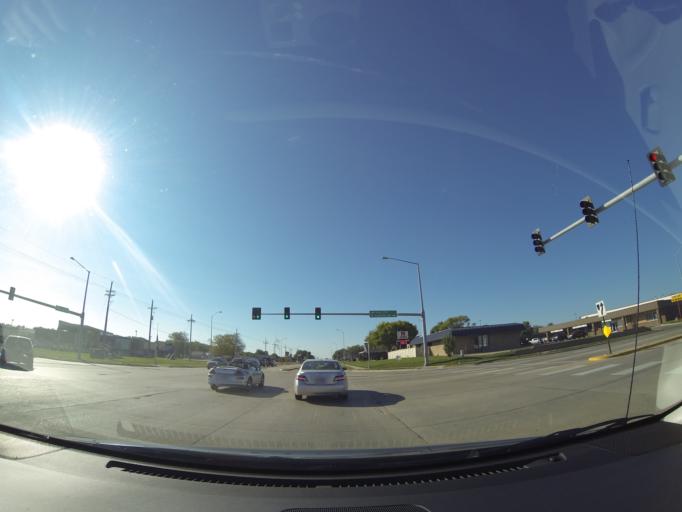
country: US
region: Nebraska
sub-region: Sarpy County
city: Gretna
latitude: 41.1471
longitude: -96.2391
